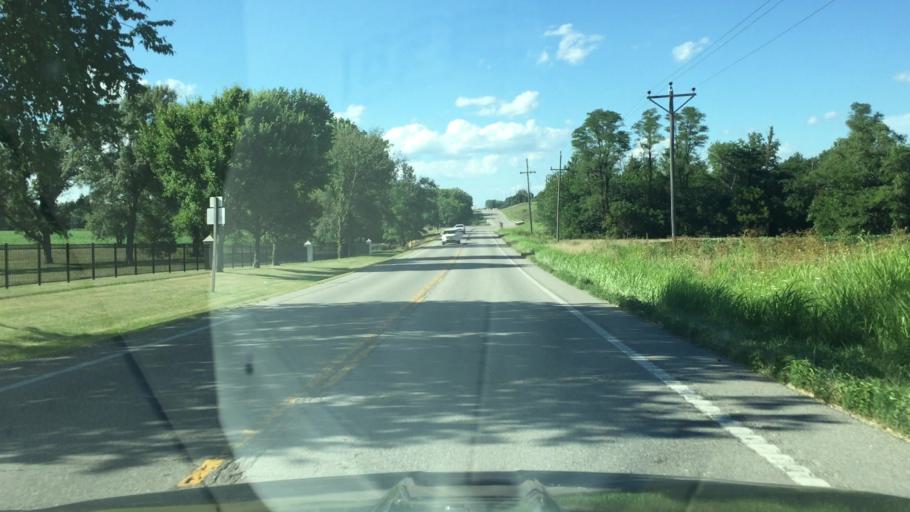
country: US
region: Missouri
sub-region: Moniteau County
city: Tipton
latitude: 38.6269
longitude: -92.7895
